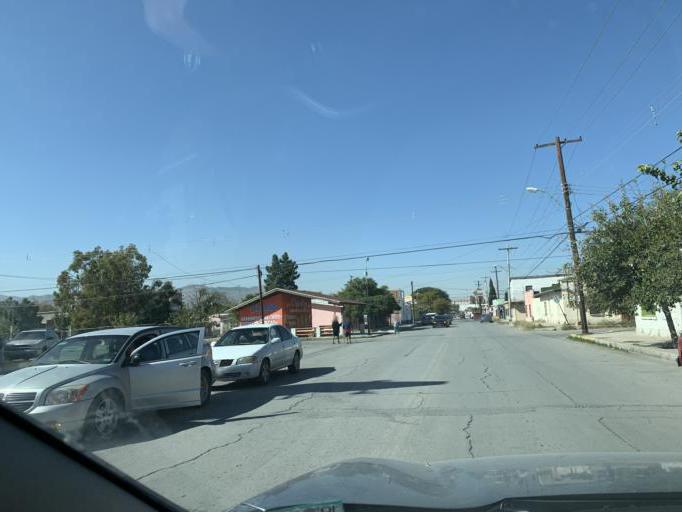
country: MX
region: Chihuahua
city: Ciudad Juarez
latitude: 31.7244
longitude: -106.4615
